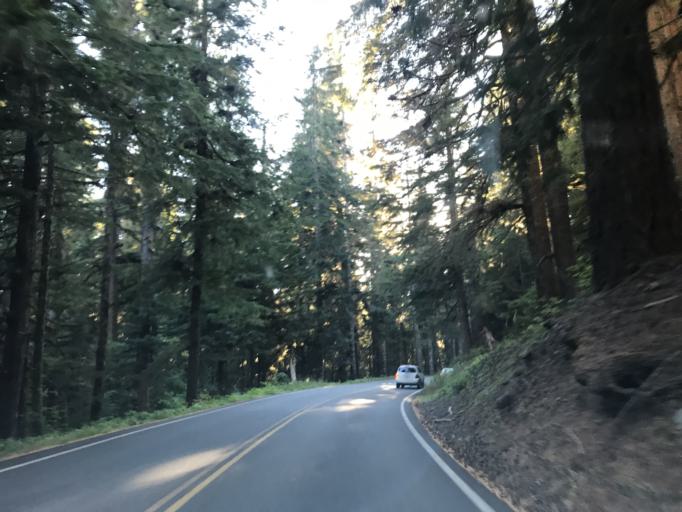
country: US
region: Washington
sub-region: Pierce County
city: Eatonville
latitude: 46.7348
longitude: -121.8467
